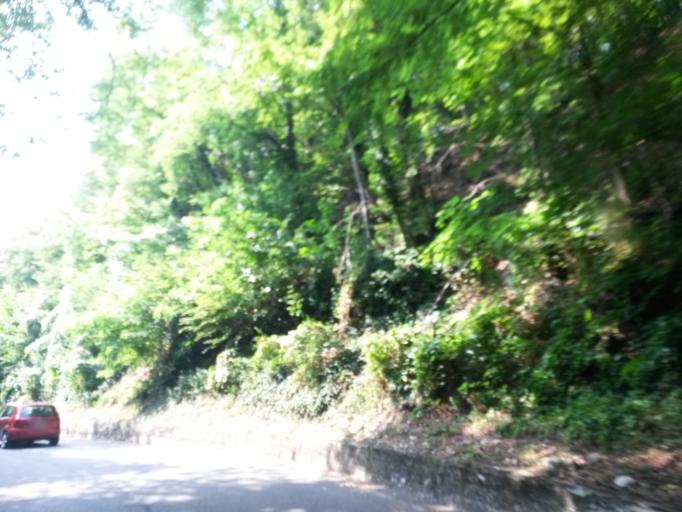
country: IT
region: Lombardy
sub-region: Provincia di Brescia
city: Gardola
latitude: 45.7343
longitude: 10.7147
